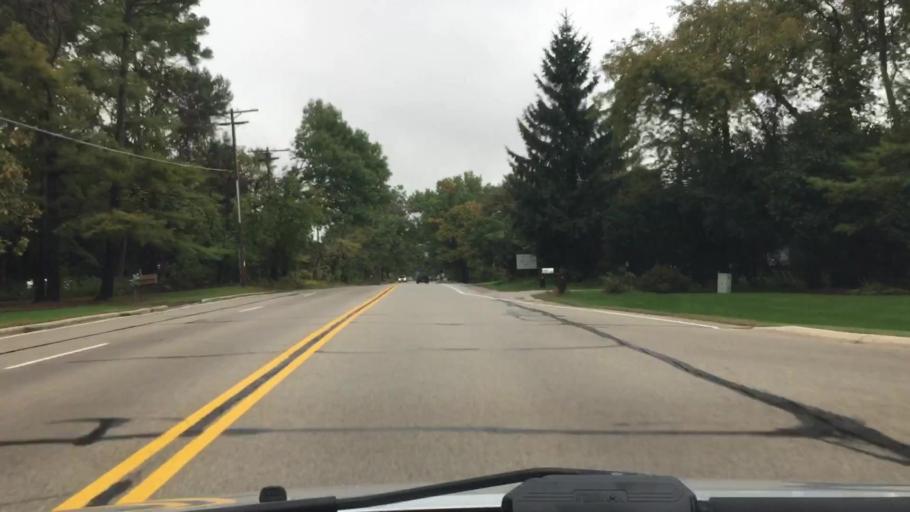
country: US
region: Wisconsin
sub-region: Waukesha County
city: Dousman
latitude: 42.9924
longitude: -88.4635
